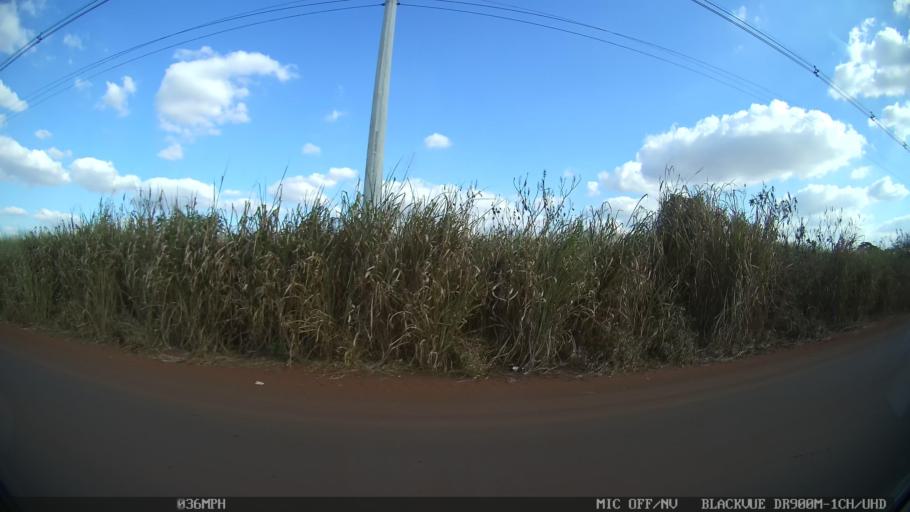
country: BR
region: Sao Paulo
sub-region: Americana
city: Americana
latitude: -22.7853
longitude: -47.3577
